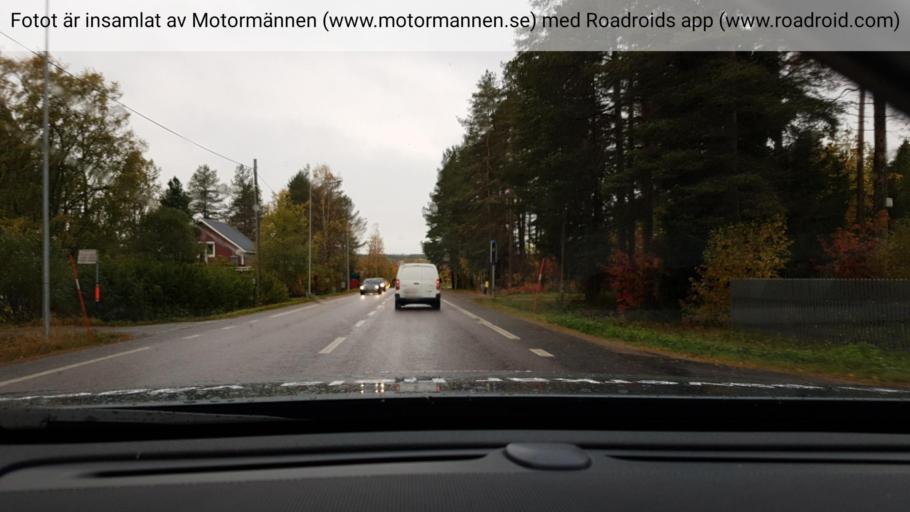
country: SE
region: Norrbotten
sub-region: Lulea Kommun
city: Bergnaset
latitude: 65.5807
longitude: 22.0676
